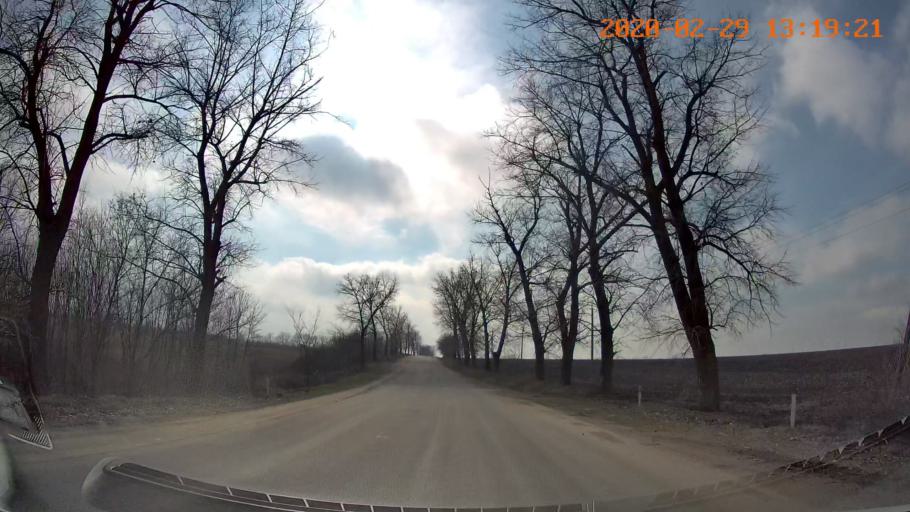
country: MD
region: Telenesti
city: Camenca
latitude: 47.9895
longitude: 28.6516
